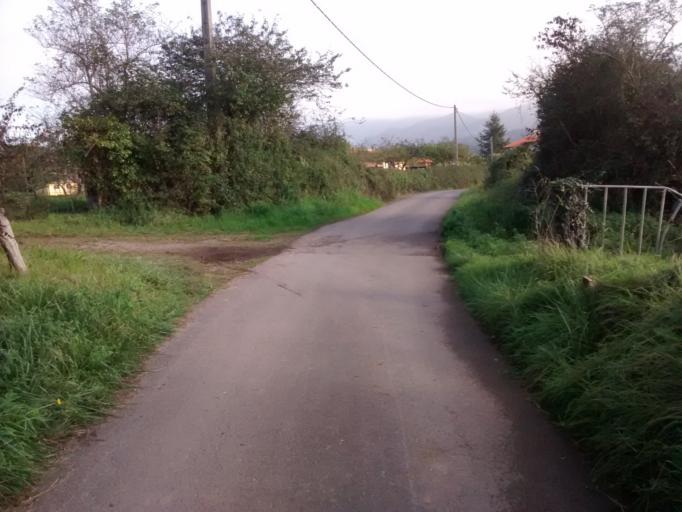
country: ES
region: Asturias
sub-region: Province of Asturias
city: Colunga
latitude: 43.4706
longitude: -5.2412
